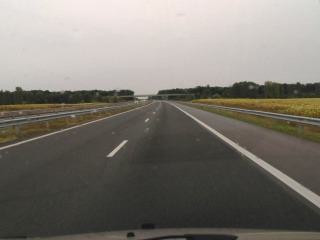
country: BG
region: Stara Zagora
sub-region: Obshtina Stara Zagora
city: Stara Zagora
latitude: 42.3512
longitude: 25.7344
